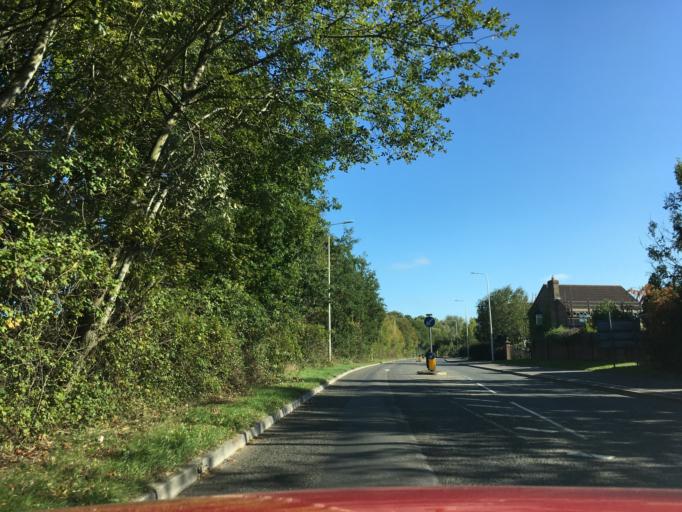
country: GB
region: England
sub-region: West Berkshire
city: Thatcham
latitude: 51.4086
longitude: -1.2451
